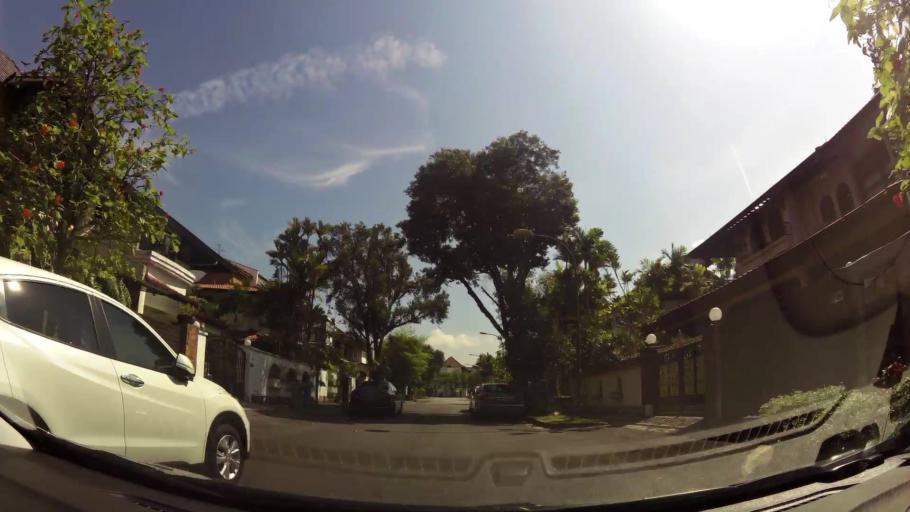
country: SG
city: Singapore
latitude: 1.3784
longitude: 103.8336
